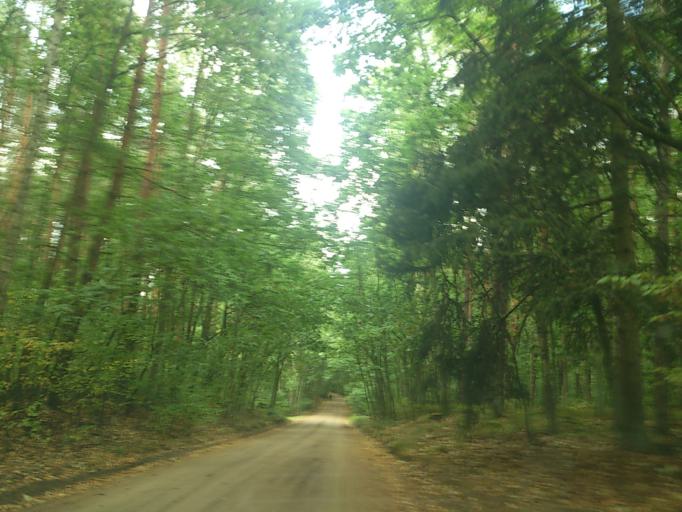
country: PL
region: Greater Poland Voivodeship
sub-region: Powiat poznanski
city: Kobylnica
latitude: 52.5428
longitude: 17.1164
